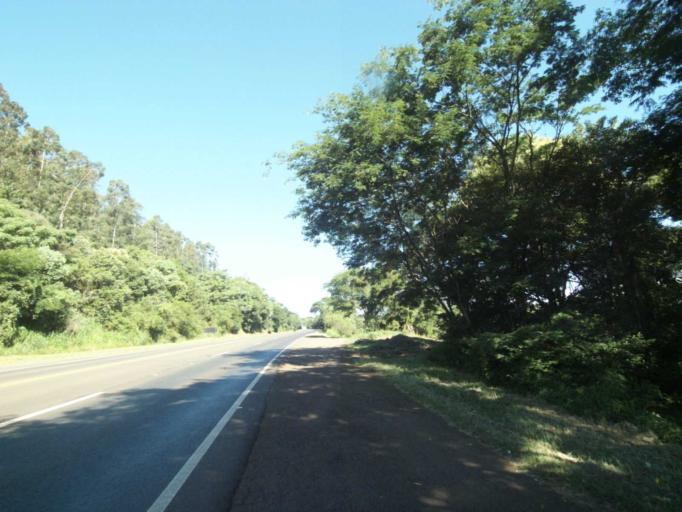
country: BR
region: Parana
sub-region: Laranjeiras Do Sul
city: Laranjeiras do Sul
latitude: -25.3782
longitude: -52.1978
